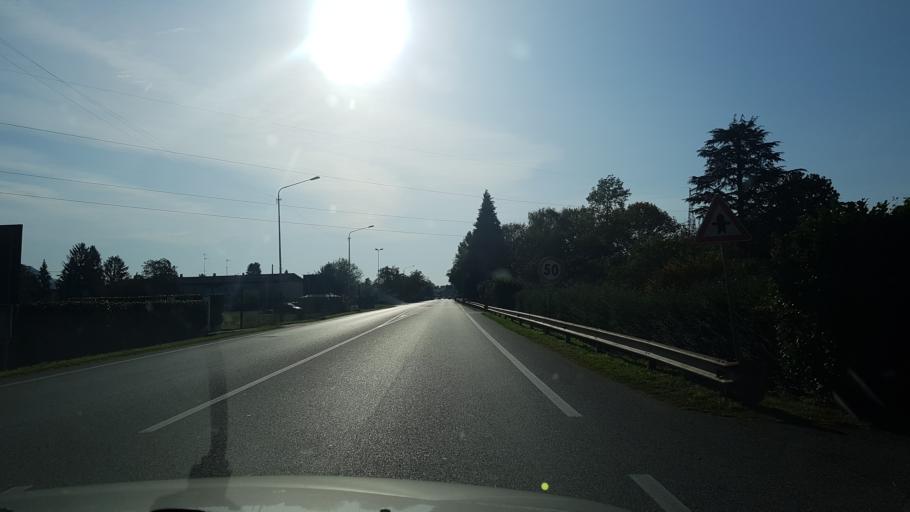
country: IT
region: Friuli Venezia Giulia
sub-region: Provincia di Udine
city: Gemona
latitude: 46.2560
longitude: 13.1118
